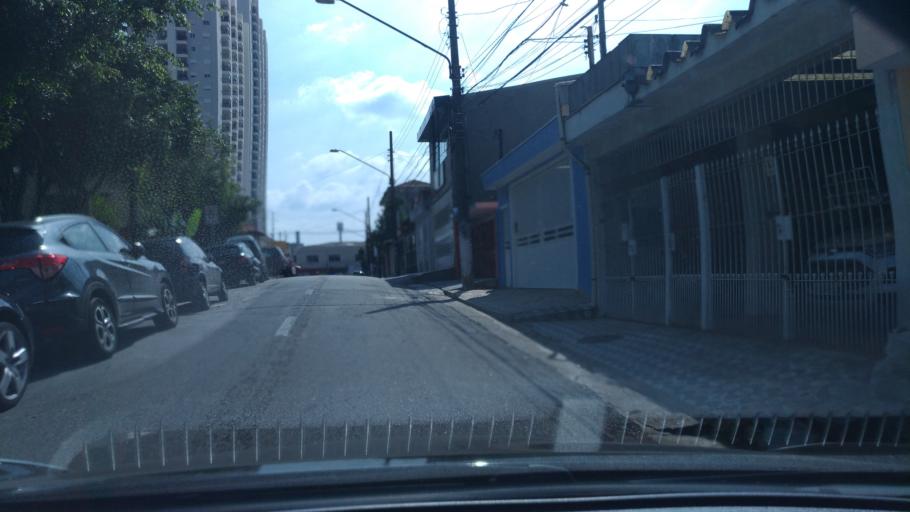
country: BR
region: Sao Paulo
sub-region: Sao Bernardo Do Campo
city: Sao Bernardo do Campo
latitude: -23.6967
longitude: -46.5828
